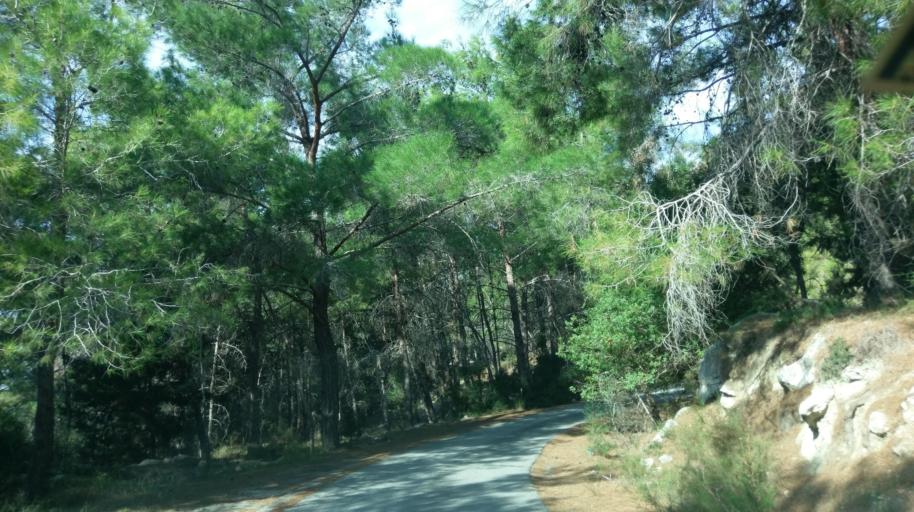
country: CY
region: Keryneia
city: Lapithos
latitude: 35.3298
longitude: 33.1144
